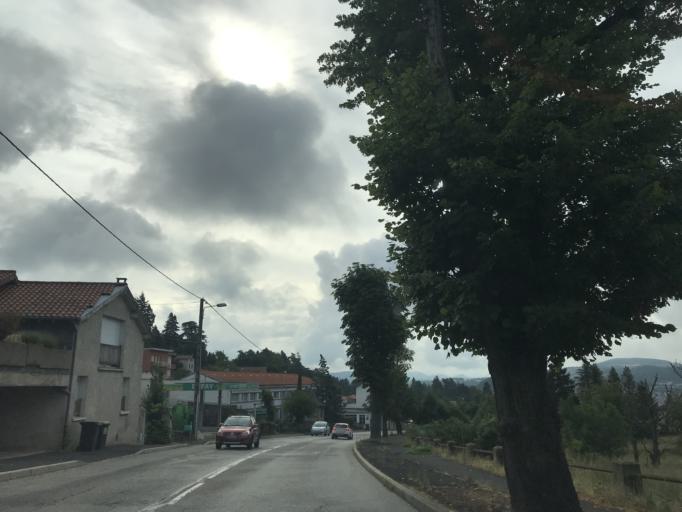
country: FR
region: Auvergne
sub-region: Departement de la Haute-Loire
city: Espaly-Saint-Marcel
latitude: 45.0556
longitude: 3.8627
